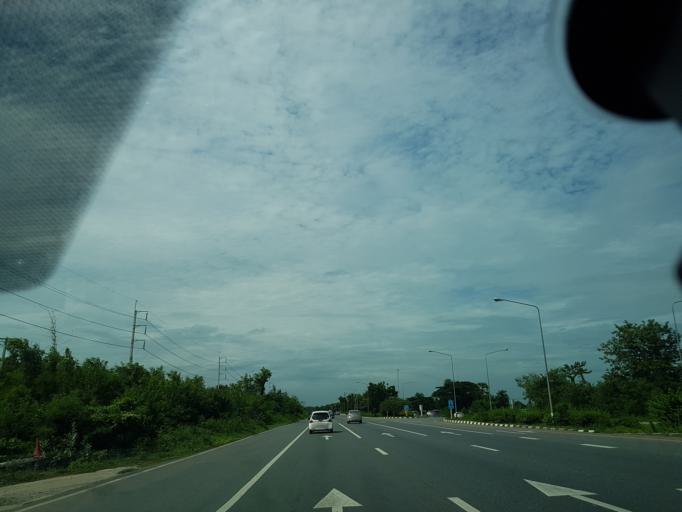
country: TH
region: Ang Thong
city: Chaiyo
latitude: 14.7121
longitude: 100.4558
